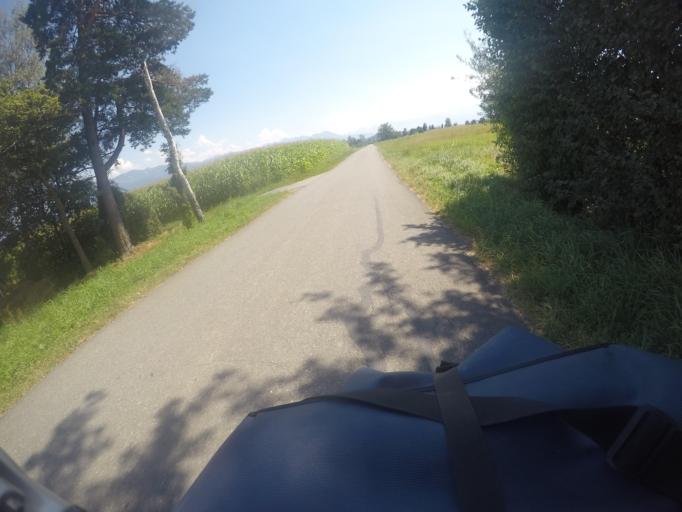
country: CH
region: Saint Gallen
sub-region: Wahlkreis Rheintal
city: Altstatten
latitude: 47.3606
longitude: 9.5699
